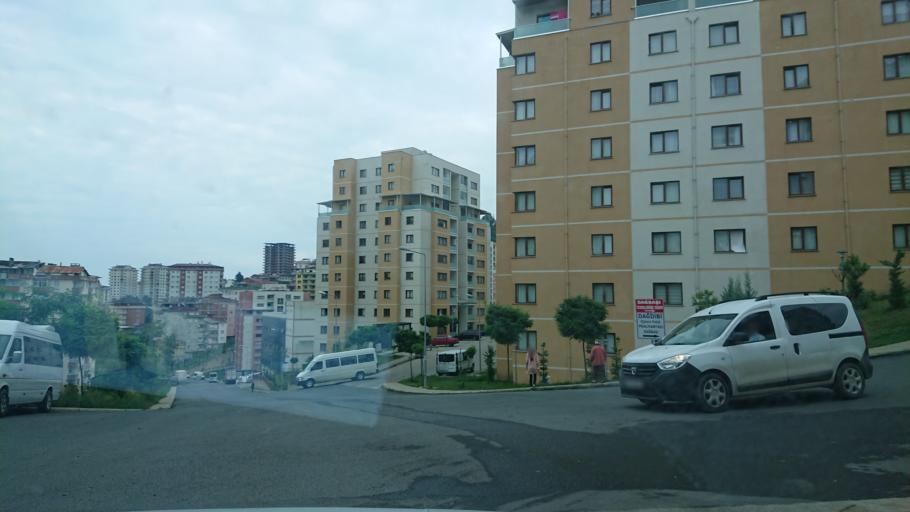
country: TR
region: Rize
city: Rize
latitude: 41.0160
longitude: 40.5134
